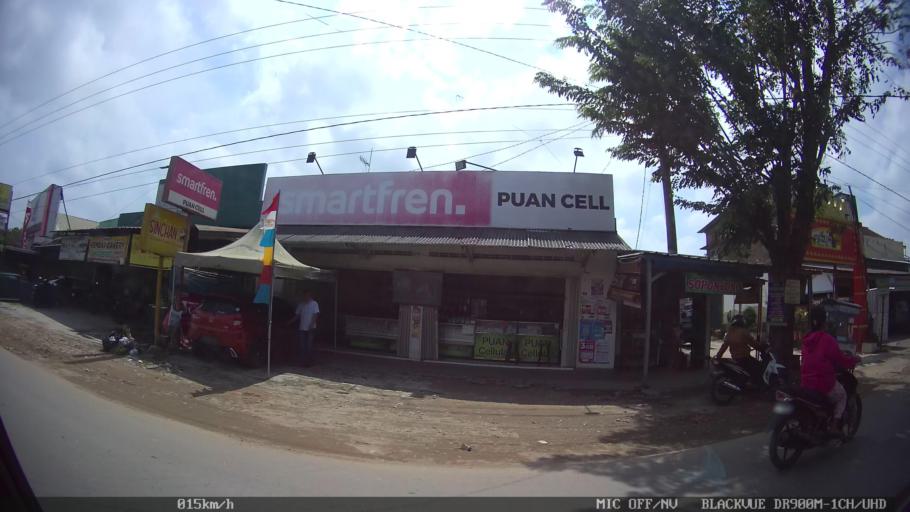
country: ID
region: Lampung
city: Kedaton
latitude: -5.3422
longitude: 105.2945
